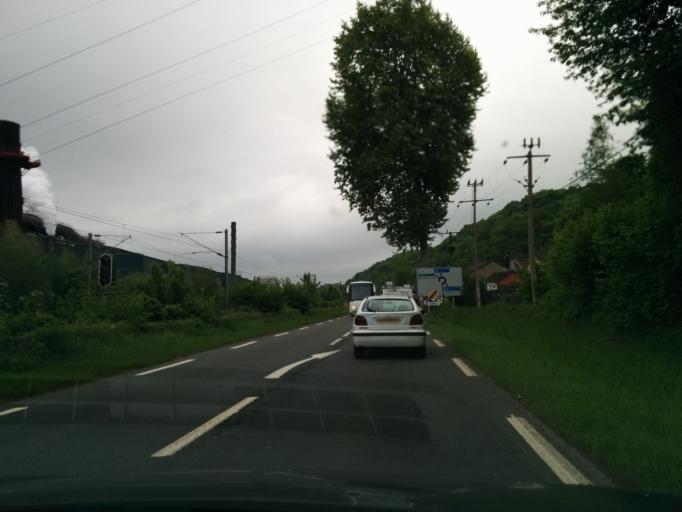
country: FR
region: Ile-de-France
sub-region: Departement des Yvelines
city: Bennecourt
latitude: 49.0329
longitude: 1.5583
